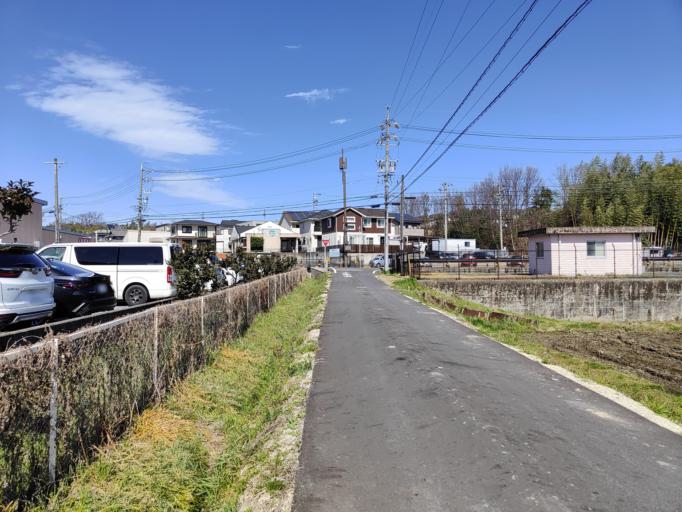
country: JP
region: Aichi
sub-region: Toyota-shi
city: Toyota
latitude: 35.1499
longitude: 137.1808
